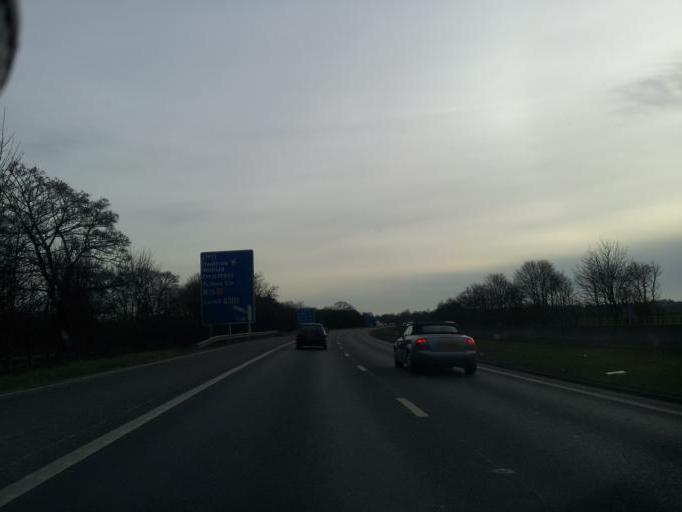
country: GB
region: England
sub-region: Hertfordshire
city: Potters Bar
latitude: 51.7058
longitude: -0.2201
